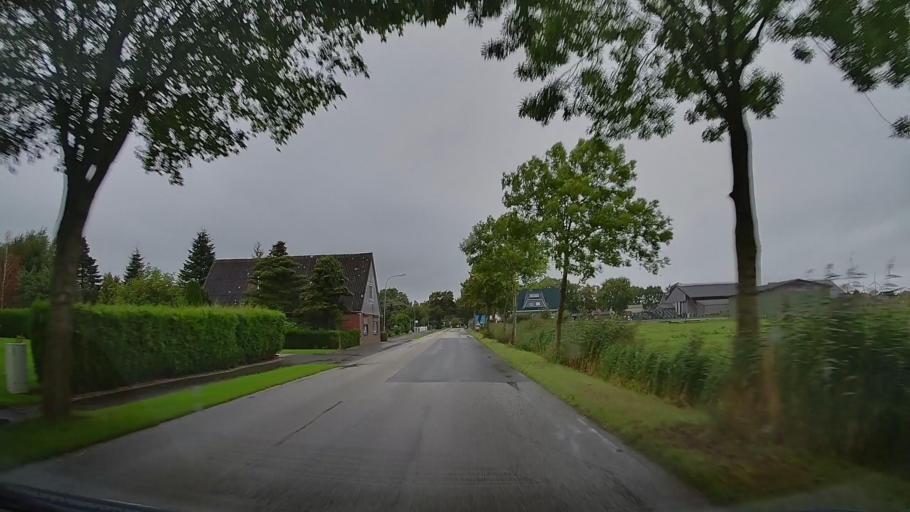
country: DE
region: Schleswig-Holstein
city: Sankt Margarethen
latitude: 53.8851
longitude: 9.2571
